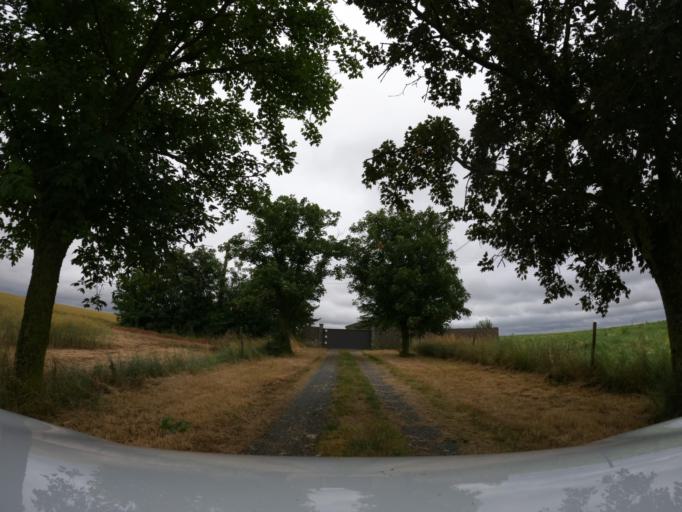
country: FR
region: Pays de la Loire
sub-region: Departement de la Vendee
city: Maillezais
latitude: 46.4069
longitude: -0.7191
